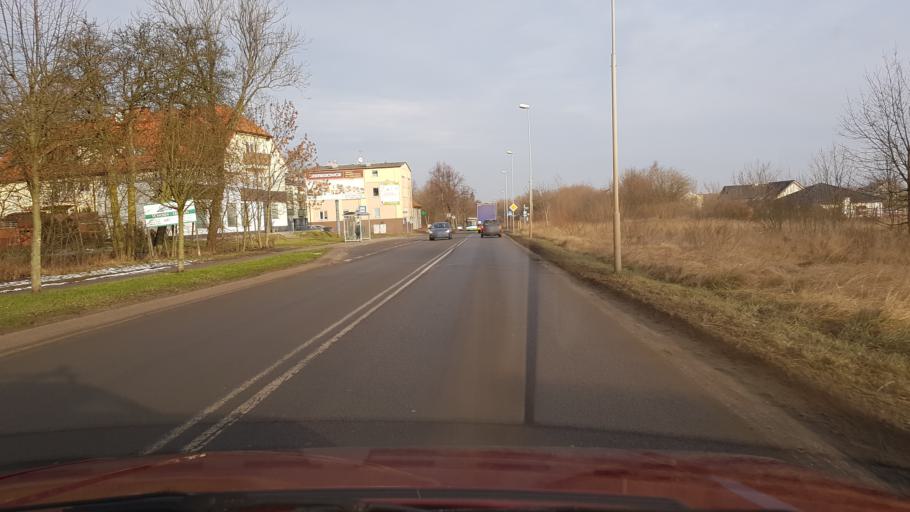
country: PL
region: West Pomeranian Voivodeship
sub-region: Szczecin
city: Szczecin
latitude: 53.4869
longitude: 14.5857
